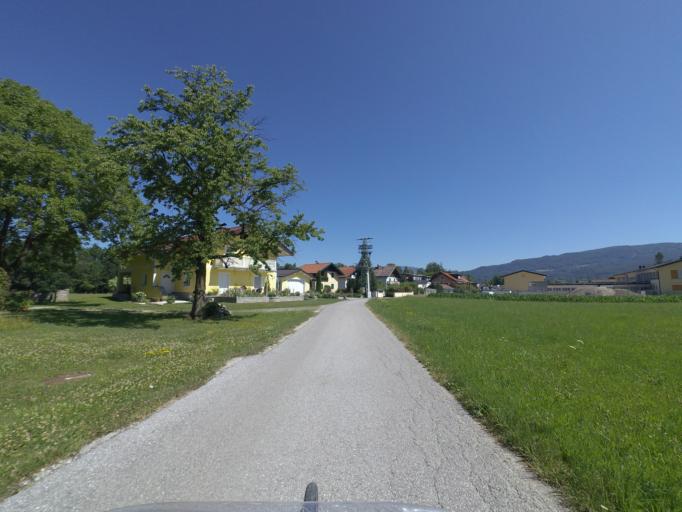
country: AT
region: Salzburg
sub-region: Politischer Bezirk Hallein
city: Puch bei Hallein
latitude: 47.7175
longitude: 13.0676
